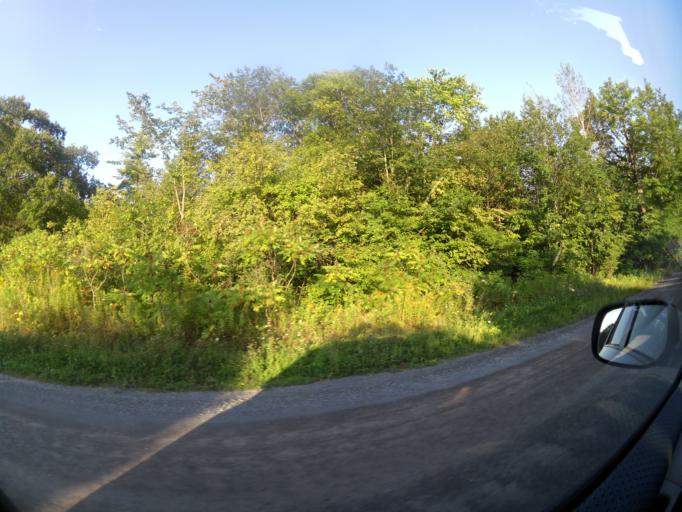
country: CA
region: Ontario
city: Clarence-Rockland
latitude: 45.5009
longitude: -75.4201
